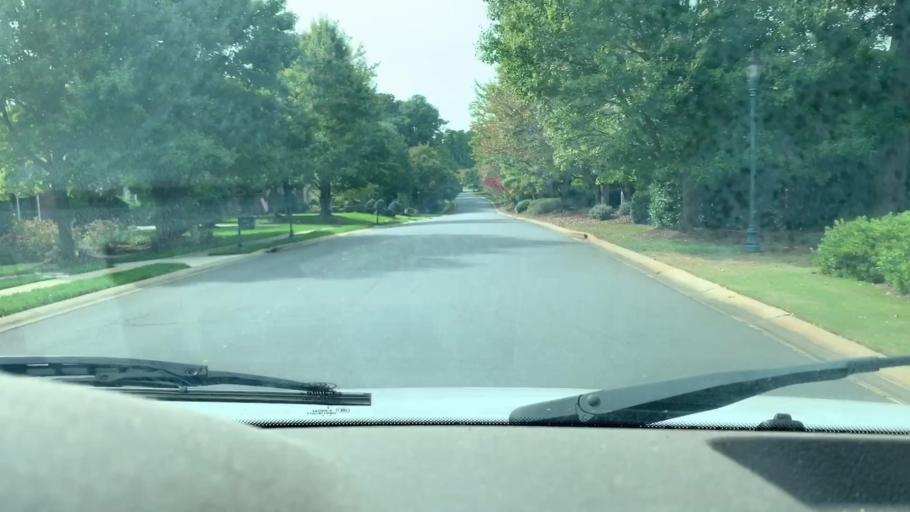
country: US
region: North Carolina
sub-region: Lincoln County
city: Westport
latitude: 35.4687
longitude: -80.9322
